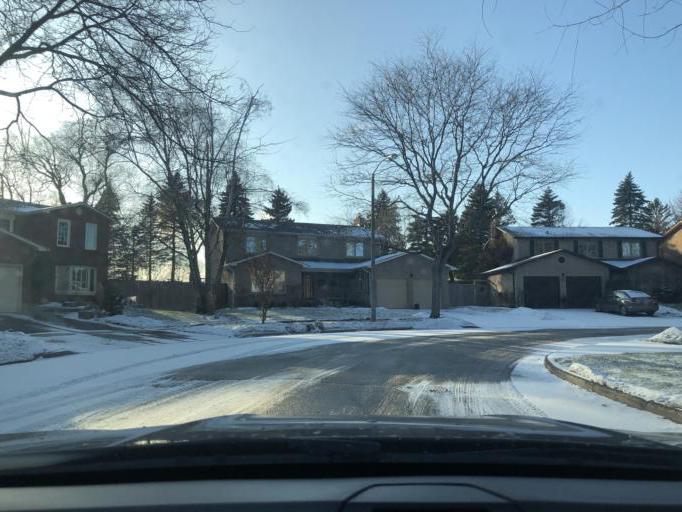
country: CA
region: Ontario
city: Scarborough
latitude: 43.7764
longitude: -79.1540
